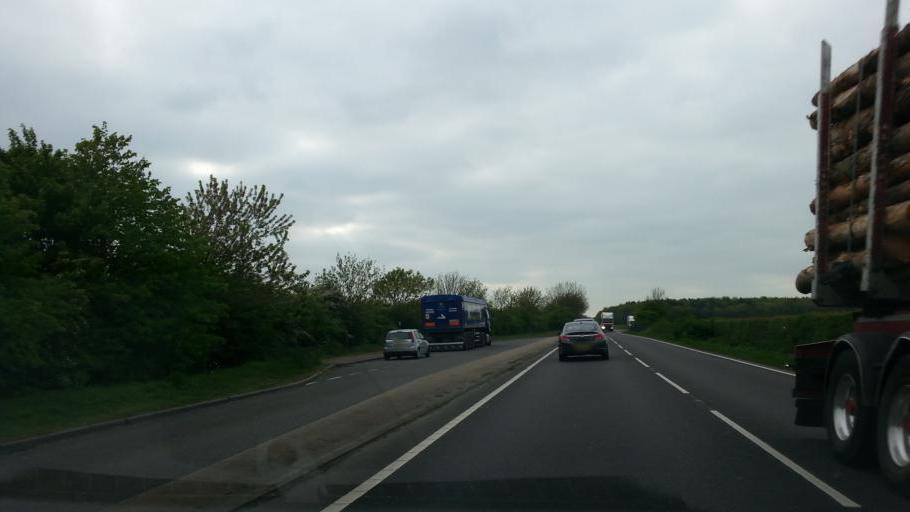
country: GB
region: England
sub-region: Lincolnshire
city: Navenby
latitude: 53.0406
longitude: -0.5432
